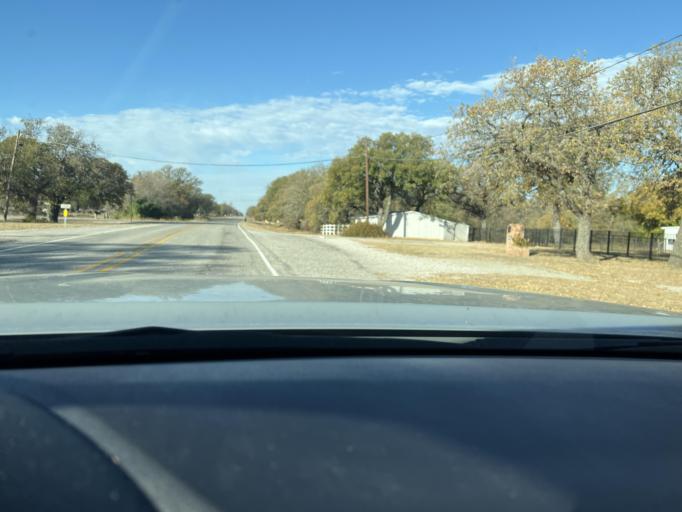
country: US
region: Texas
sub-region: Eastland County
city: Ranger
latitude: 32.4193
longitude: -98.7373
